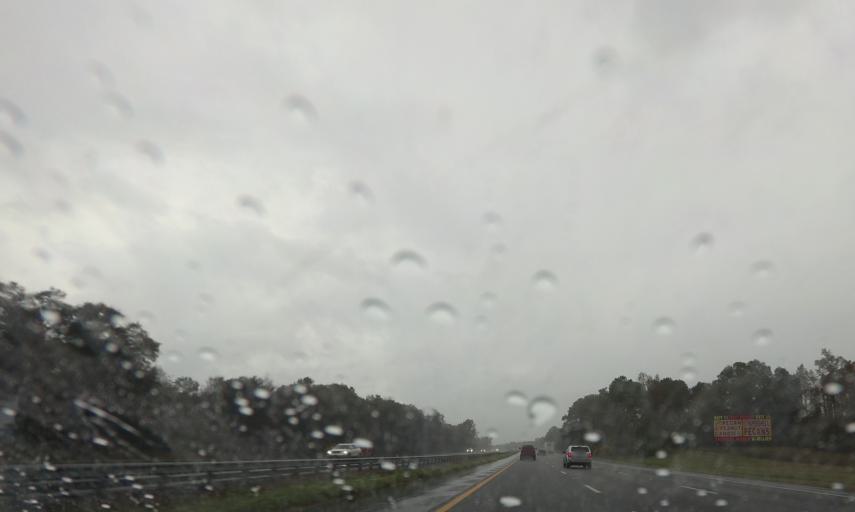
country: US
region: Florida
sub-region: Hamilton County
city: Jasper
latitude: 30.5375
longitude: -83.0719
